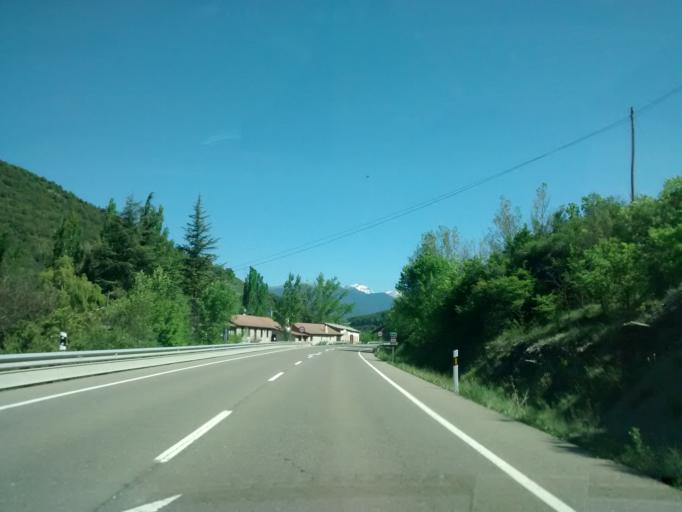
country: ES
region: Aragon
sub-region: Provincia de Huesca
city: Jaca
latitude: 42.5974
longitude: -0.5437
